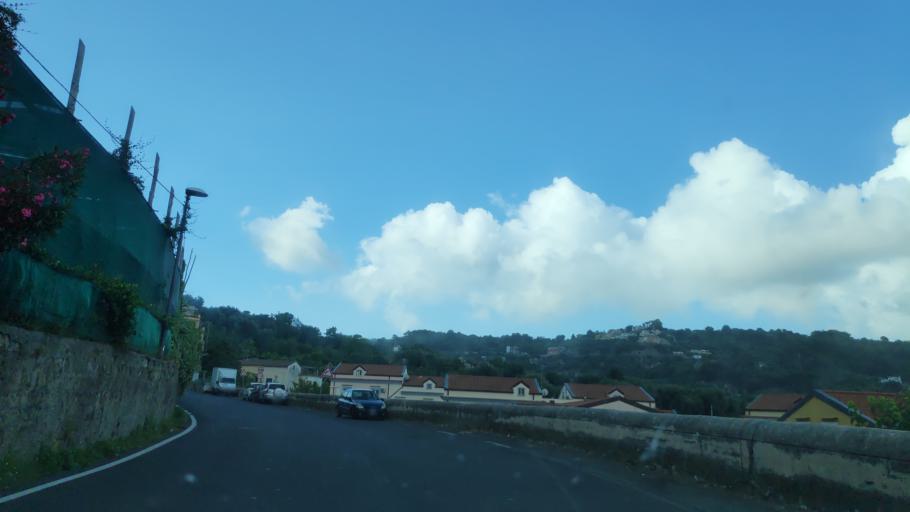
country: IT
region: Campania
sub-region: Provincia di Napoli
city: Piano di Sorrento
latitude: 40.6281
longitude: 14.4239
